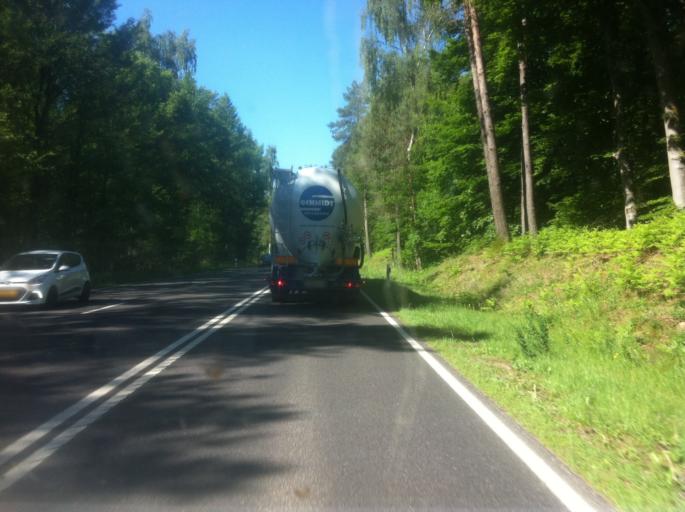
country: LU
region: Grevenmacher
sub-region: Canton d'Echternach
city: Waldbillig
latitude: 49.7439
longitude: 6.2937
